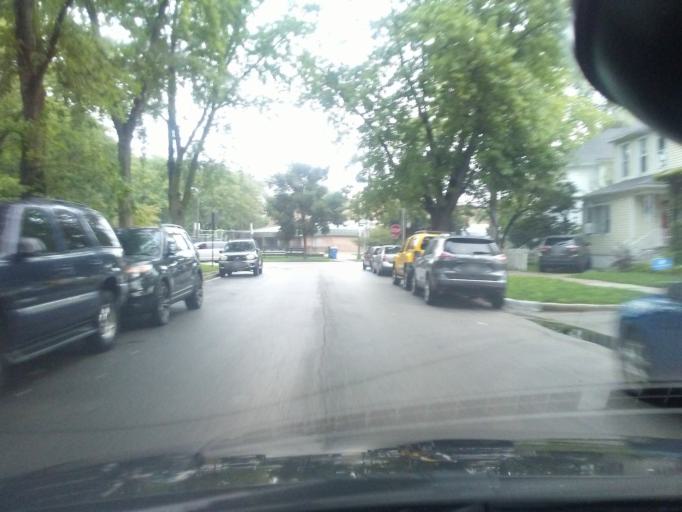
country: US
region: Illinois
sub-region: Cook County
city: Evanston
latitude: 42.0142
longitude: -87.6782
